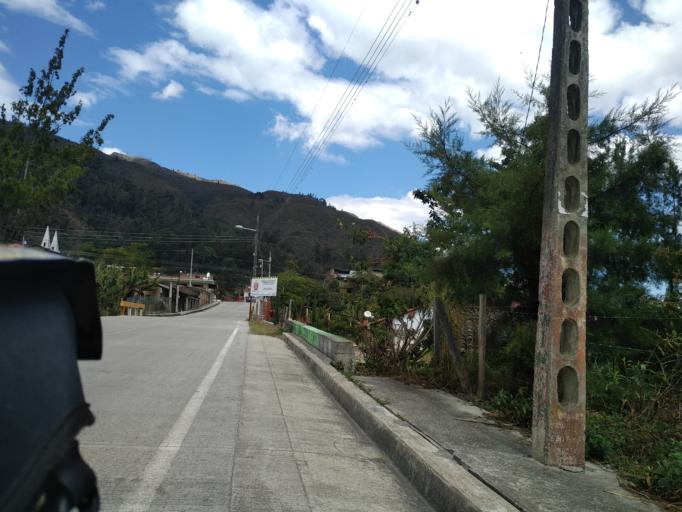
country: EC
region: Zamora-Chinchipe
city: Zamora
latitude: -4.3639
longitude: -79.1750
